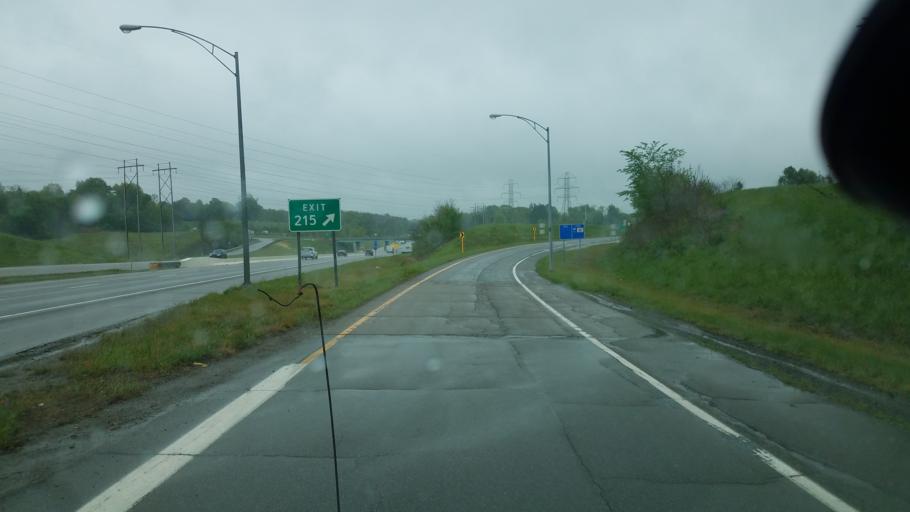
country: US
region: Ohio
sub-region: Belmont County
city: Saint Clairsville
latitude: 40.0770
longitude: -80.9320
